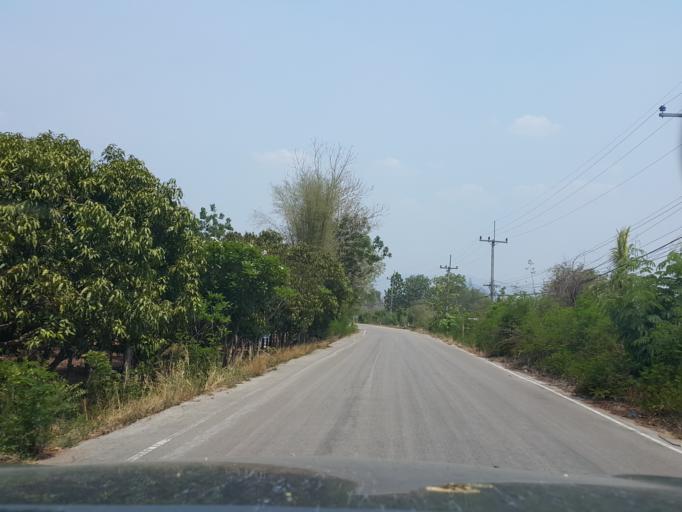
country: TH
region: Lampang
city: Mae Phrik
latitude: 17.5343
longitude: 99.1455
